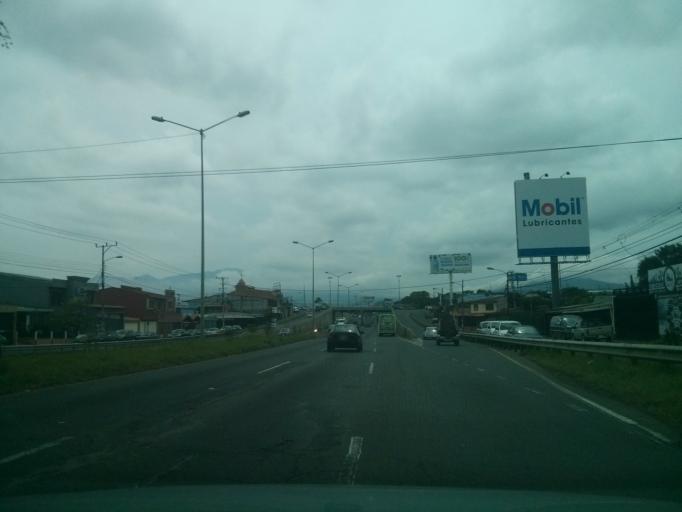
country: CR
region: San Jose
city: Alajuelita
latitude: 9.9103
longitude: -84.0881
